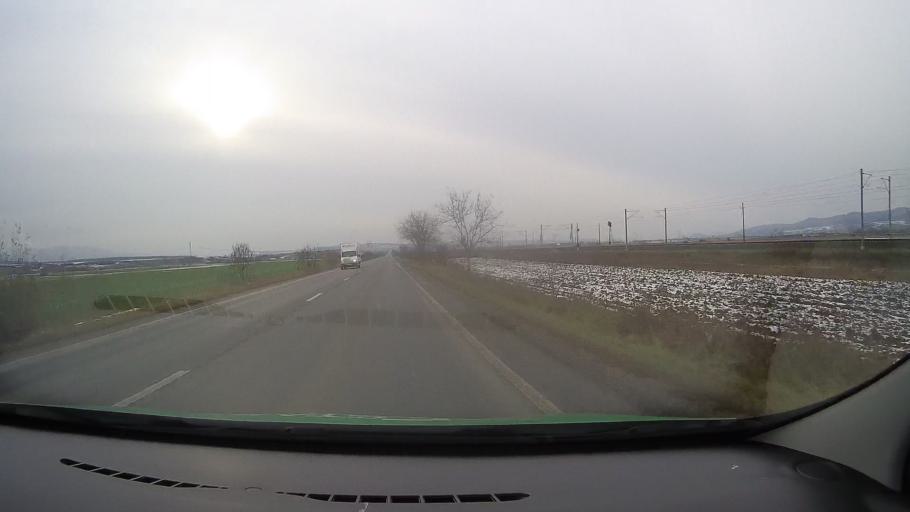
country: RO
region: Hunedoara
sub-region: Comuna Geoagiu
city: Geoagiu
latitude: 45.8805
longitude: 23.2442
